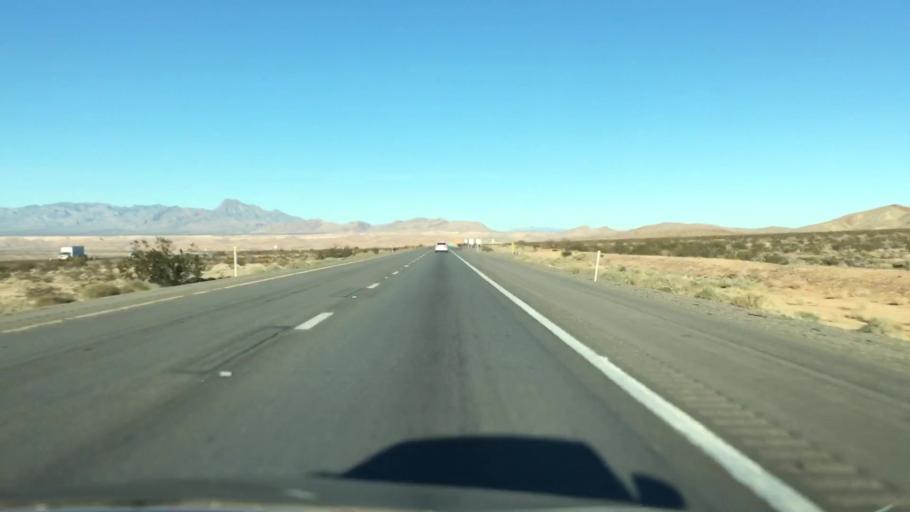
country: US
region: Nevada
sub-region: Clark County
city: Moapa Town
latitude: 36.6242
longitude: -114.6131
